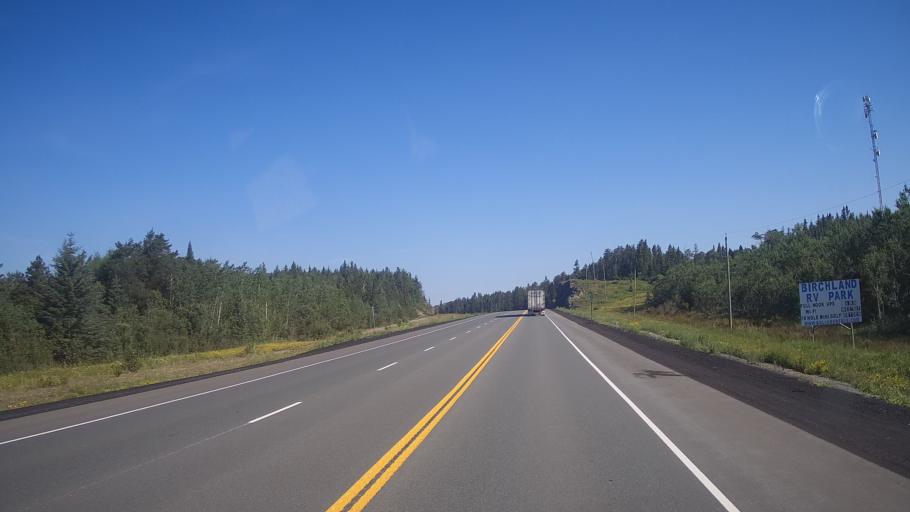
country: CA
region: Ontario
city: Dryden
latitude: 49.6379
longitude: -92.4408
